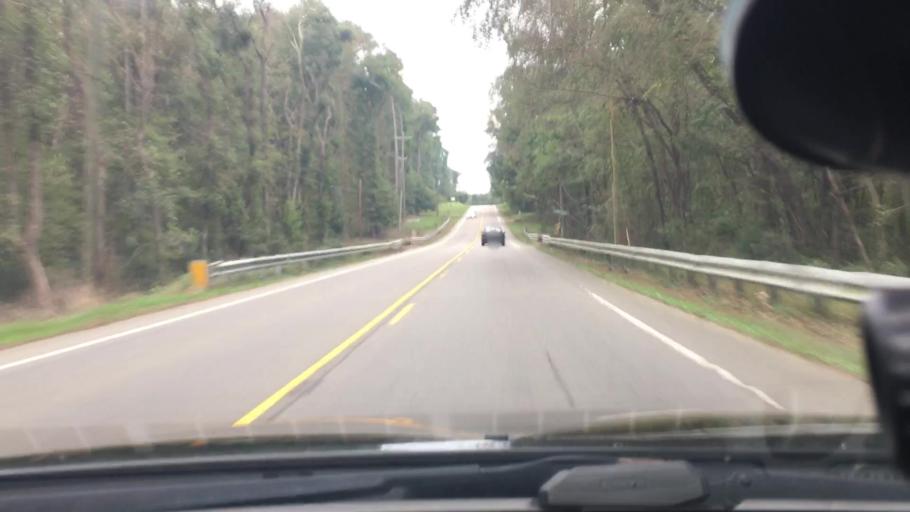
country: US
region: North Carolina
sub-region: Moore County
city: Robbins
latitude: 35.4041
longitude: -79.5674
